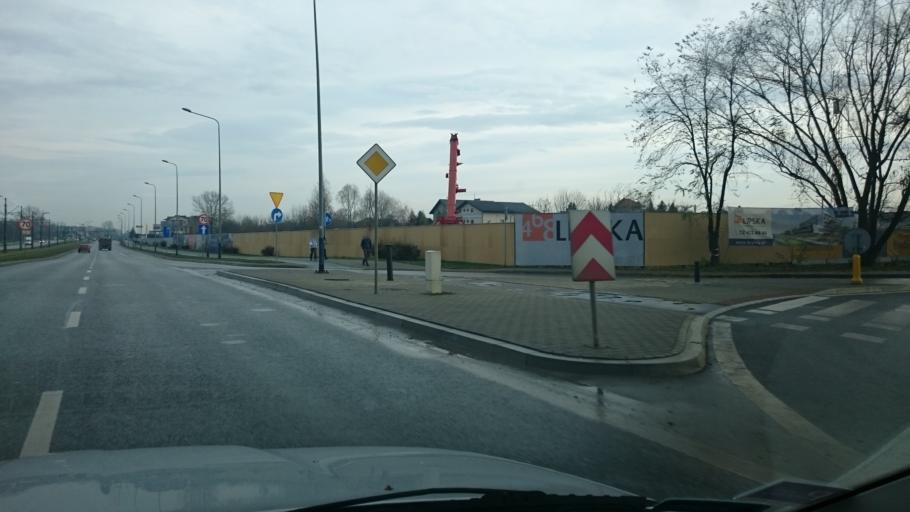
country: PL
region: Lesser Poland Voivodeship
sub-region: Krakow
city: Krakow
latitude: 50.0406
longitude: 19.9845
